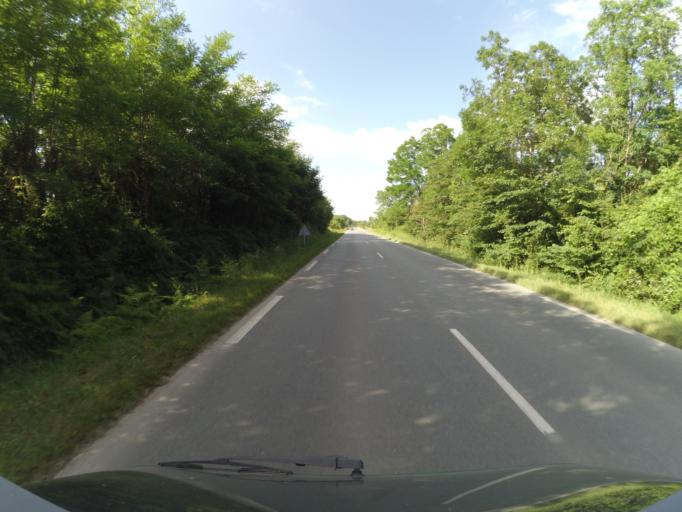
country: FR
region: Poitou-Charentes
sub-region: Departement de la Charente-Maritime
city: Le Gua
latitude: 45.7637
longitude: -0.9407
